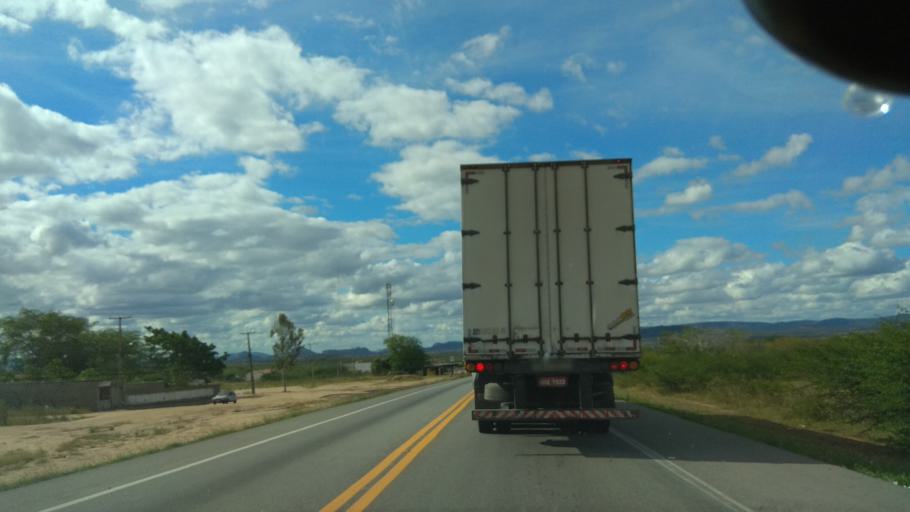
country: BR
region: Bahia
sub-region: Amargosa
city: Amargosa
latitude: -12.8580
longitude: -39.8492
